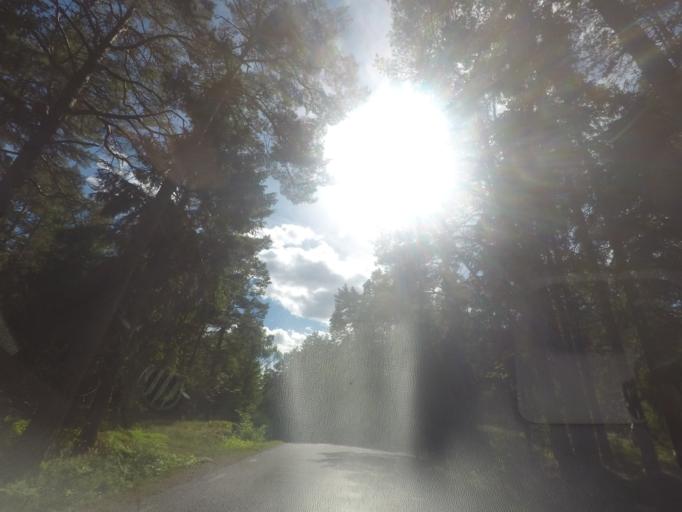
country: SE
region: Stockholm
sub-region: Norrtalje Kommun
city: Arno
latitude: 60.1852
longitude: 18.7401
